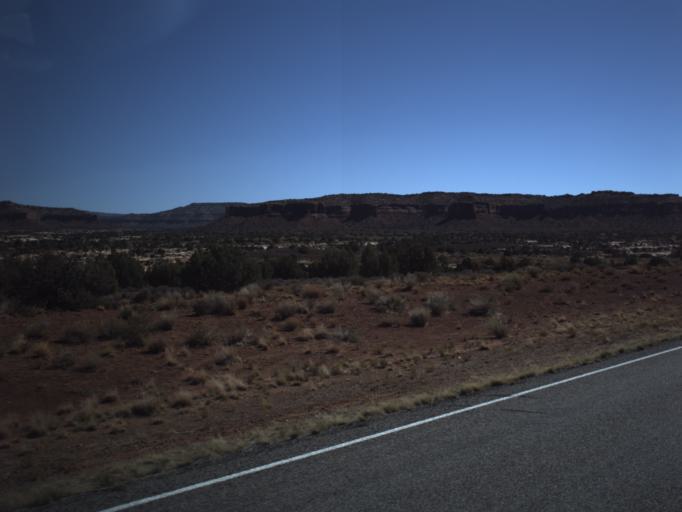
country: US
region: Utah
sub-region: San Juan County
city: Blanding
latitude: 37.7036
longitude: -110.2376
